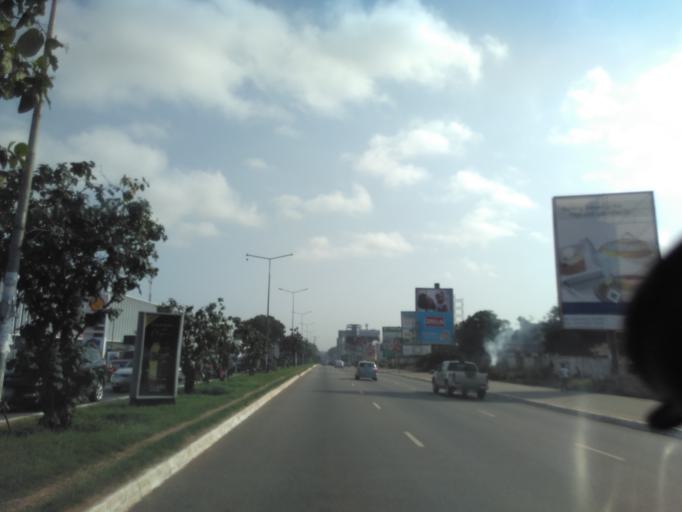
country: GH
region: Greater Accra
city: Accra
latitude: 5.5939
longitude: -0.1803
